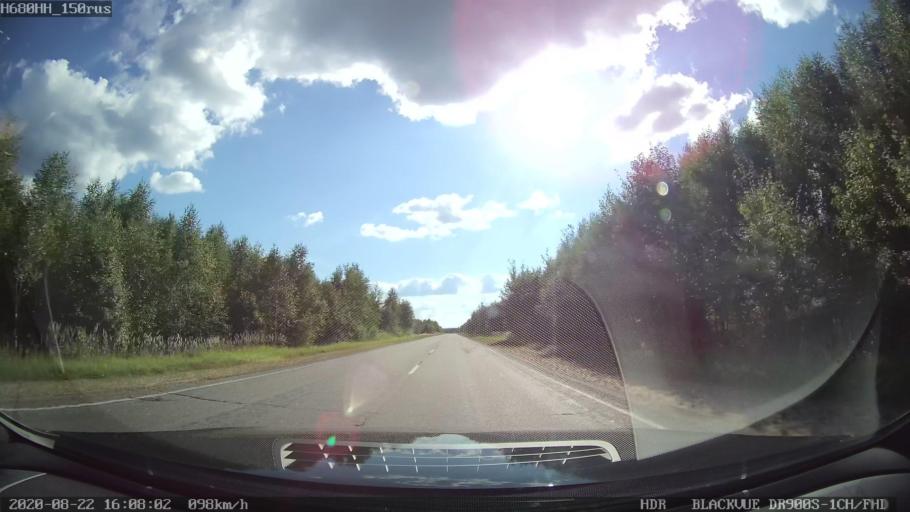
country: RU
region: Tverskaya
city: Rameshki
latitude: 57.5450
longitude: 36.3049
